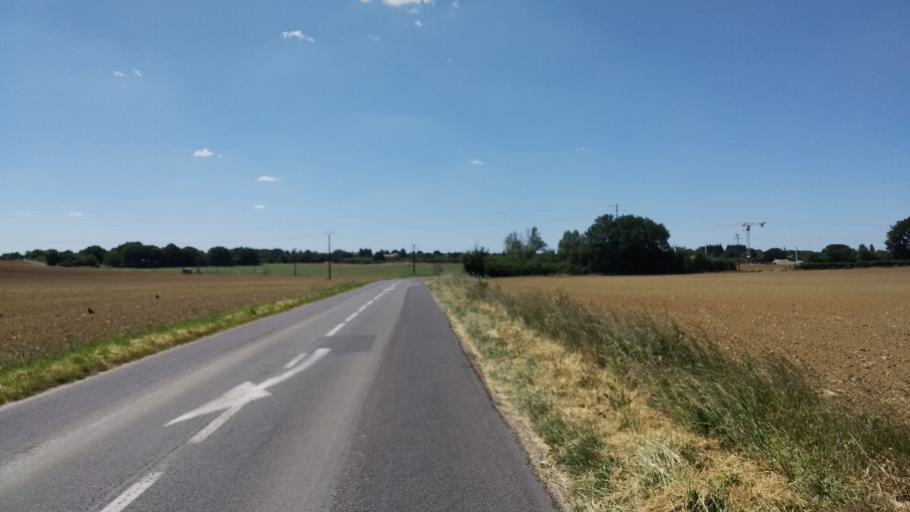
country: FR
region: Poitou-Charentes
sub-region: Departement de la Vienne
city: Biard
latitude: 46.5984
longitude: 0.2982
